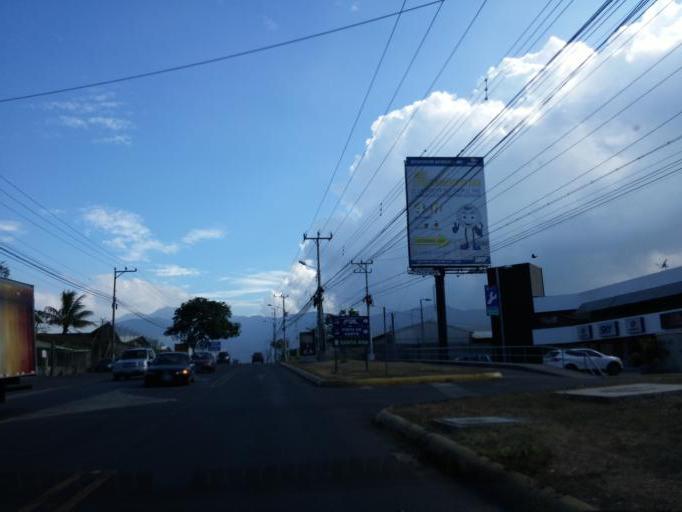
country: CR
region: Heredia
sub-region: Canton de Belen
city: San Antonio
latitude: 9.9636
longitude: -84.1983
